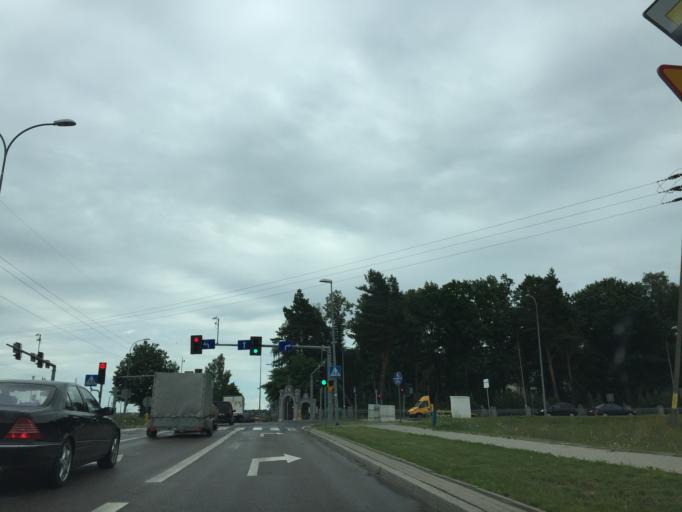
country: PL
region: Podlasie
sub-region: Bialystok
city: Bialystok
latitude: 53.1083
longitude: 23.2102
